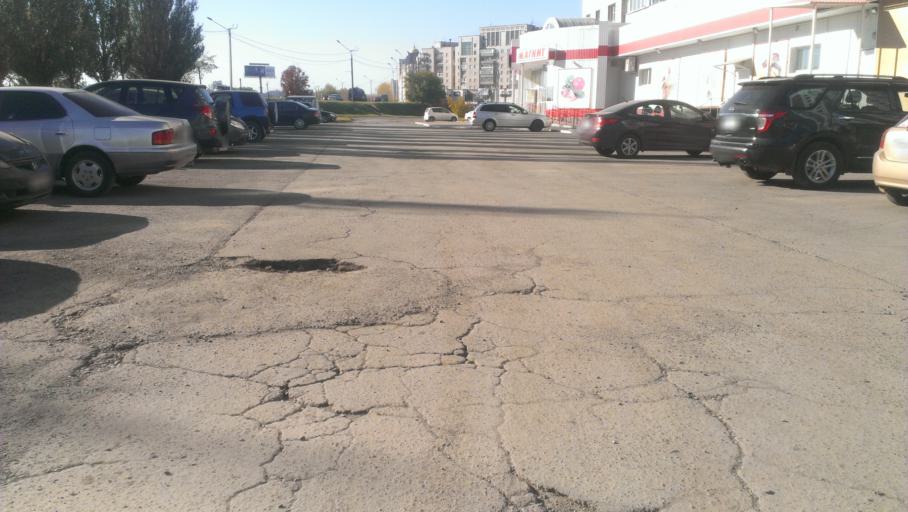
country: RU
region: Altai Krai
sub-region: Gorod Barnaulskiy
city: Barnaul
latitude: 53.3424
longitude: 83.6984
